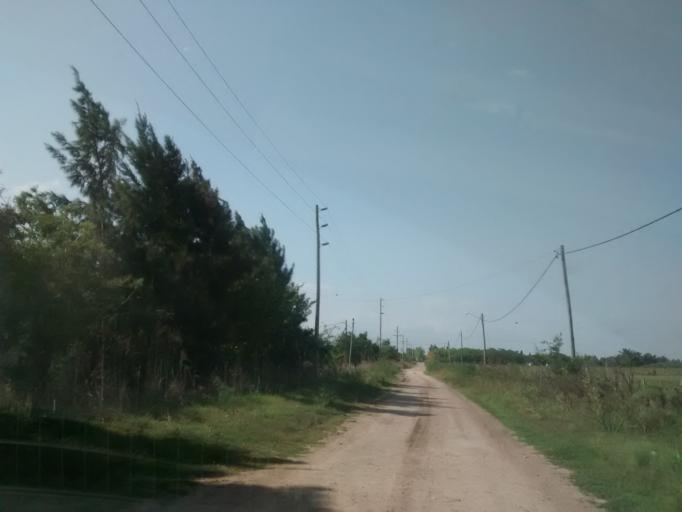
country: AR
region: Buenos Aires
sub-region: Partido de La Plata
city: La Plata
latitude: -35.0068
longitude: -57.9036
